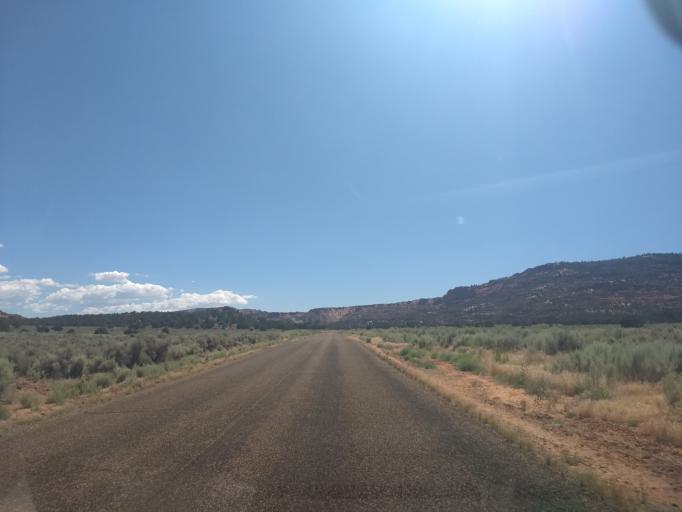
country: US
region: Utah
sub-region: Washington County
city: Hildale
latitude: 37.0118
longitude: -112.8462
